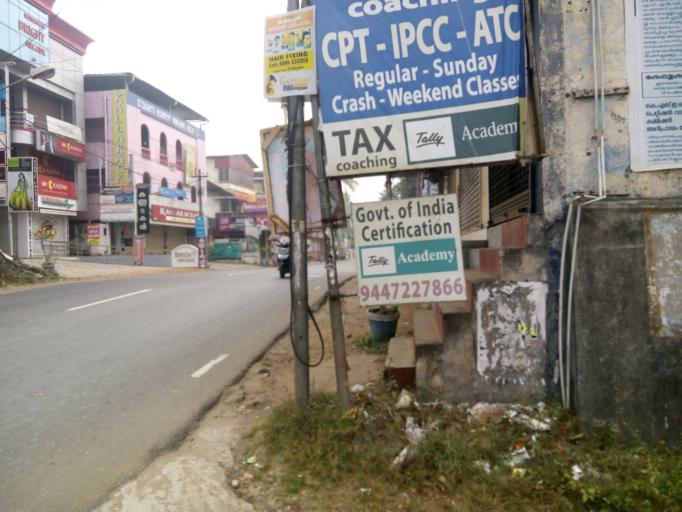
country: IN
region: Kerala
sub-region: Kottayam
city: Lalam
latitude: 9.7097
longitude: 76.6763
